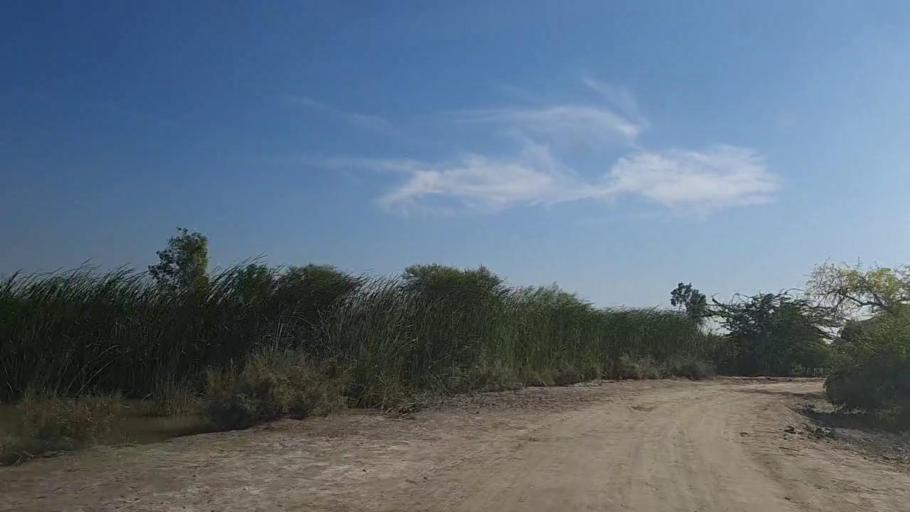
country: PK
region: Sindh
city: Mirpur Batoro
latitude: 24.7574
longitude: 68.3004
